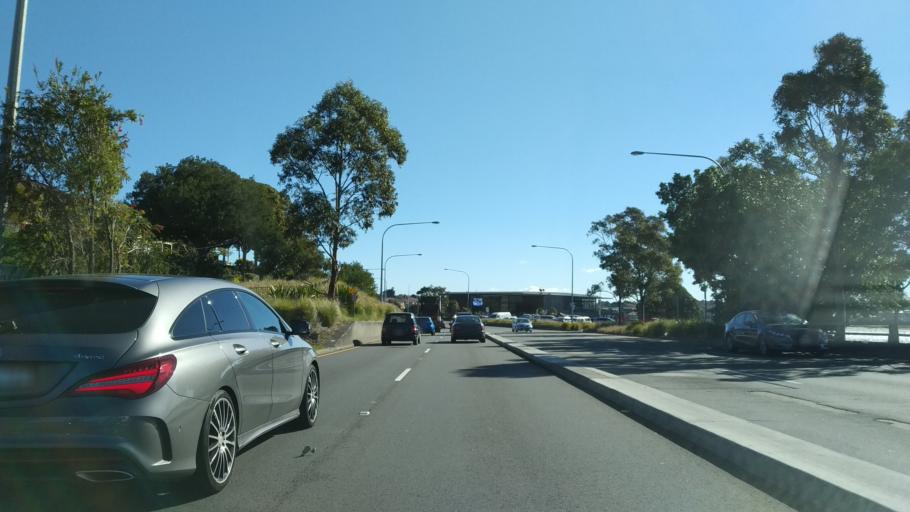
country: AU
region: New South Wales
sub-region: Leichhardt
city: Leichhardt
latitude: -33.8714
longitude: 151.1490
